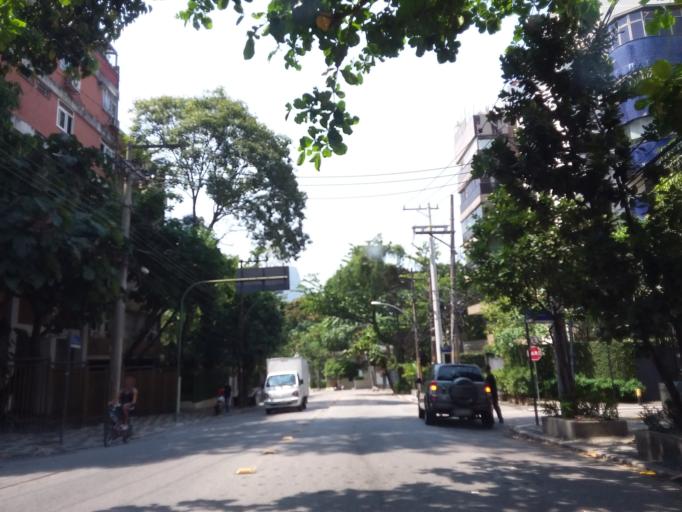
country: BR
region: Rio de Janeiro
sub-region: Rio De Janeiro
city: Rio de Janeiro
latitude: -22.9805
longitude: -43.2352
